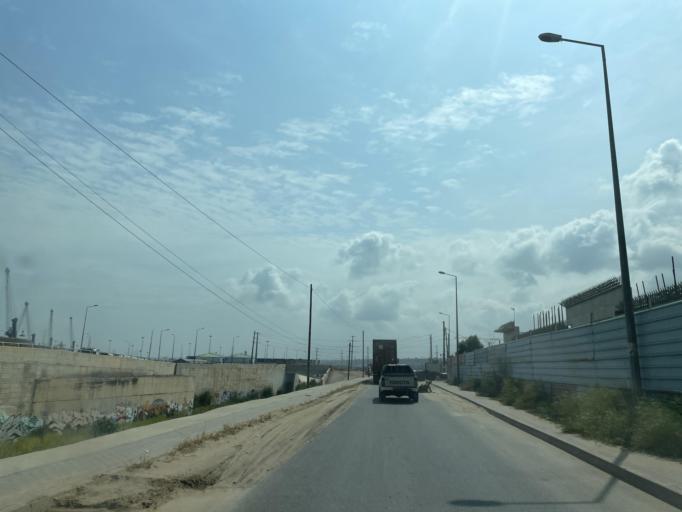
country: AO
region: Luanda
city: Luanda
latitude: -8.8036
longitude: 13.2484
